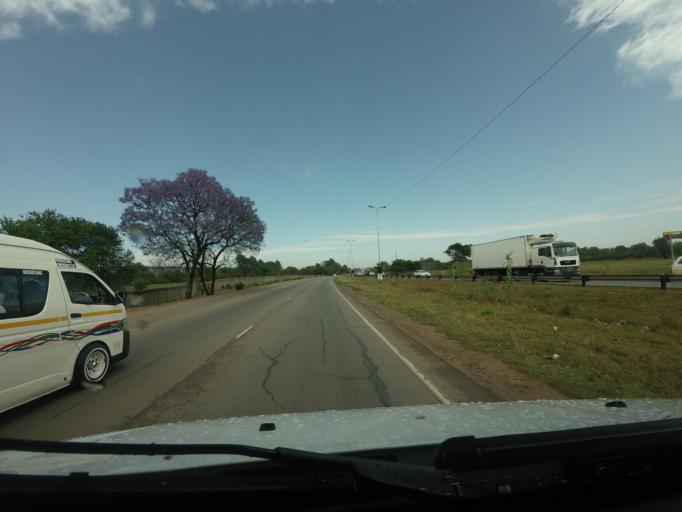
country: ZA
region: Gauteng
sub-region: City of Tshwane Metropolitan Municipality
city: Pretoria
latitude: -25.6859
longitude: 28.2895
